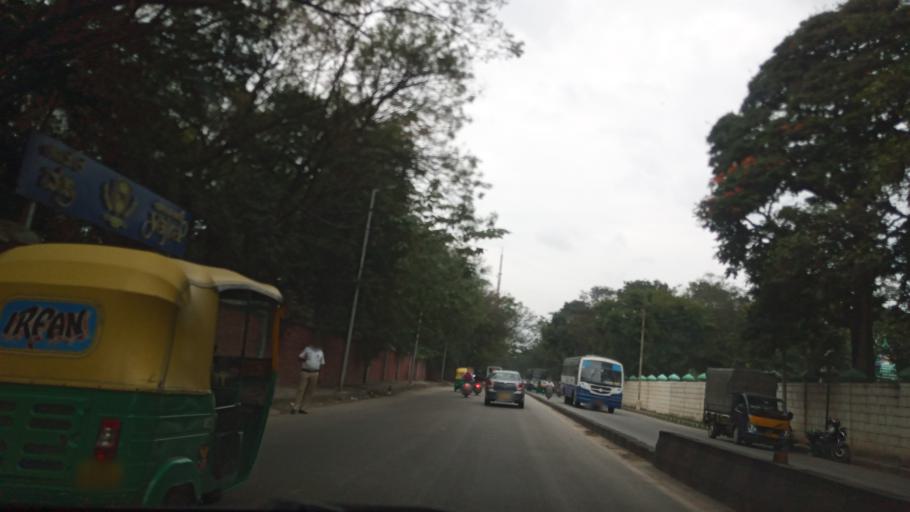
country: IN
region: Karnataka
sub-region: Bangalore Urban
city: Bangalore
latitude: 13.0018
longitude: 77.5944
